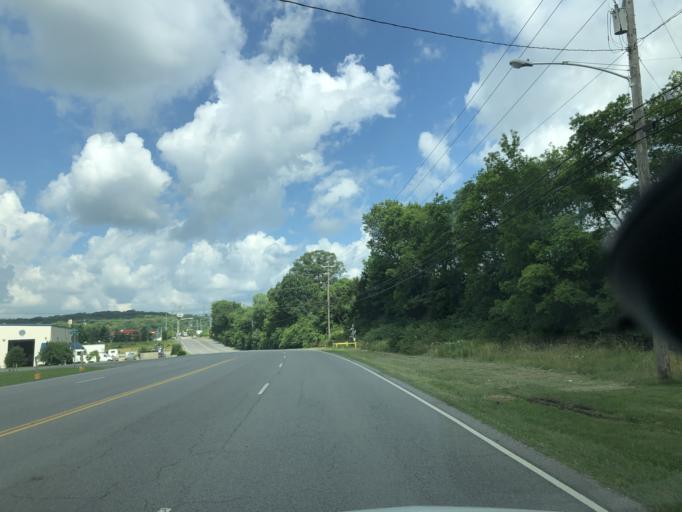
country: US
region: Tennessee
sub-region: Rutherford County
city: La Vergne
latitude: 36.0161
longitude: -86.6152
